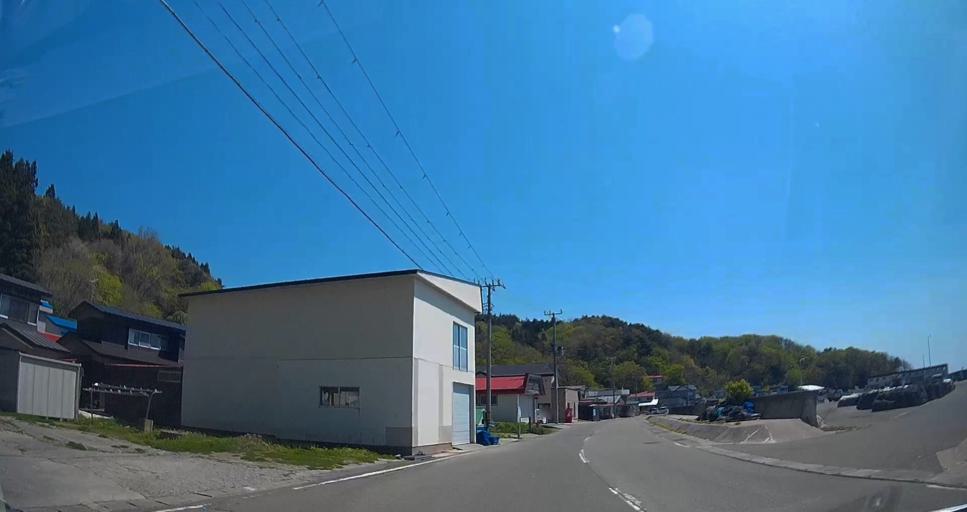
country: JP
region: Aomori
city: Aomori Shi
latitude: 41.1300
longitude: 140.8054
